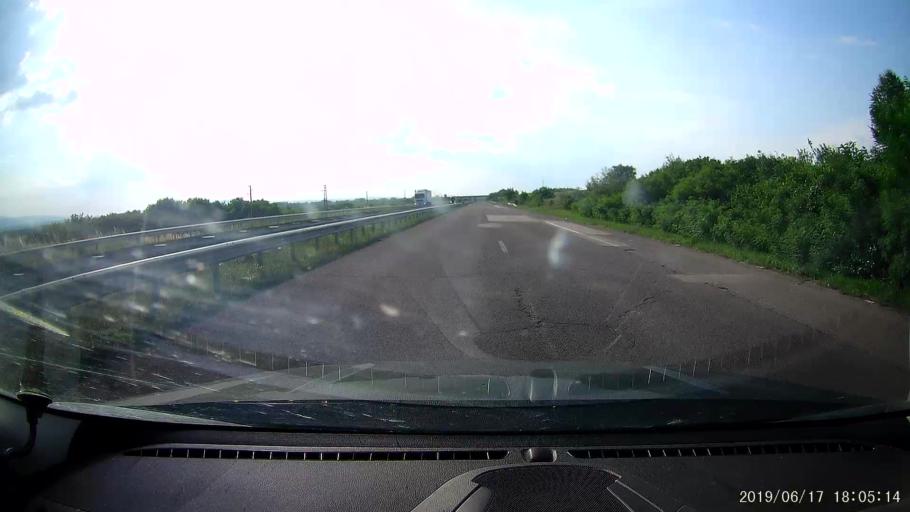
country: BG
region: Khaskovo
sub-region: Obshtina Svilengrad
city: Svilengrad
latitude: 41.7959
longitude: 26.1800
